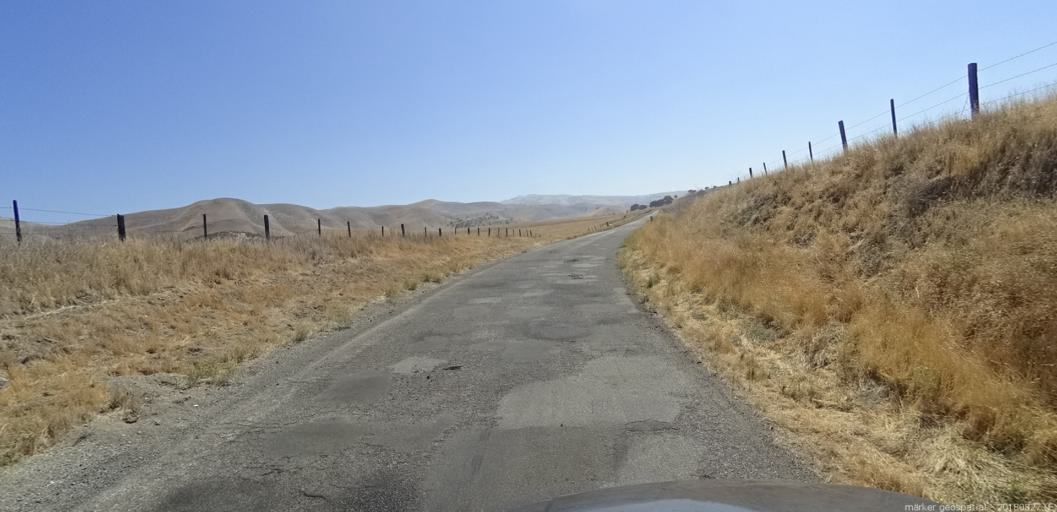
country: US
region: California
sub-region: Monterey County
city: King City
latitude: 36.2952
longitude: -120.9865
